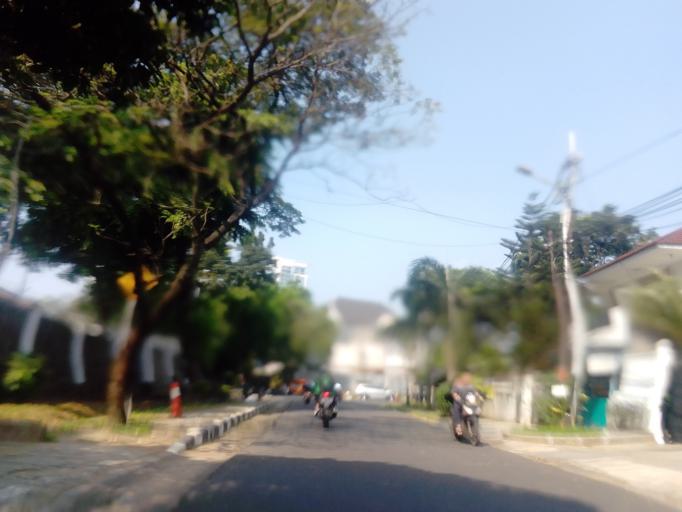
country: ID
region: Jakarta Raya
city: Jakarta
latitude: -6.2544
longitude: 106.8061
